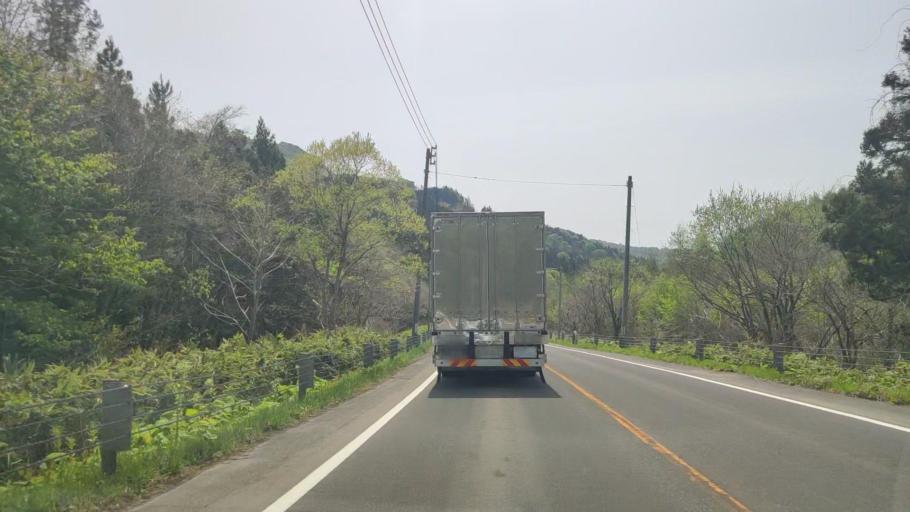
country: JP
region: Aomori
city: Aomori Shi
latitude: 40.7809
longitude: 141.0318
